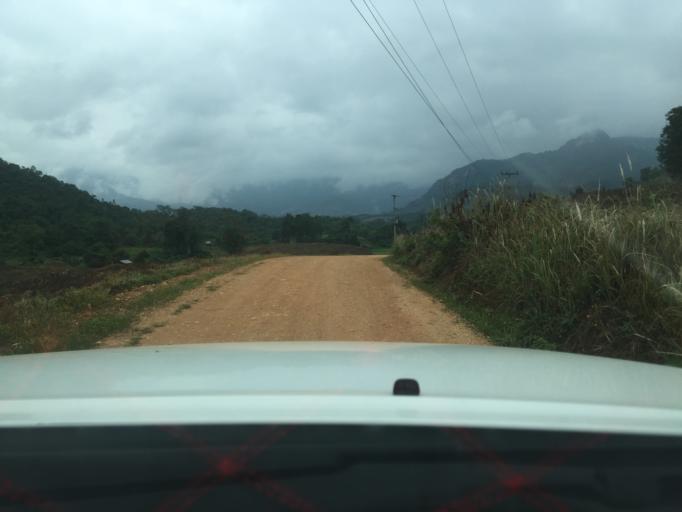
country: TH
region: Phayao
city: Phu Sang
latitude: 19.7309
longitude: 100.4808
